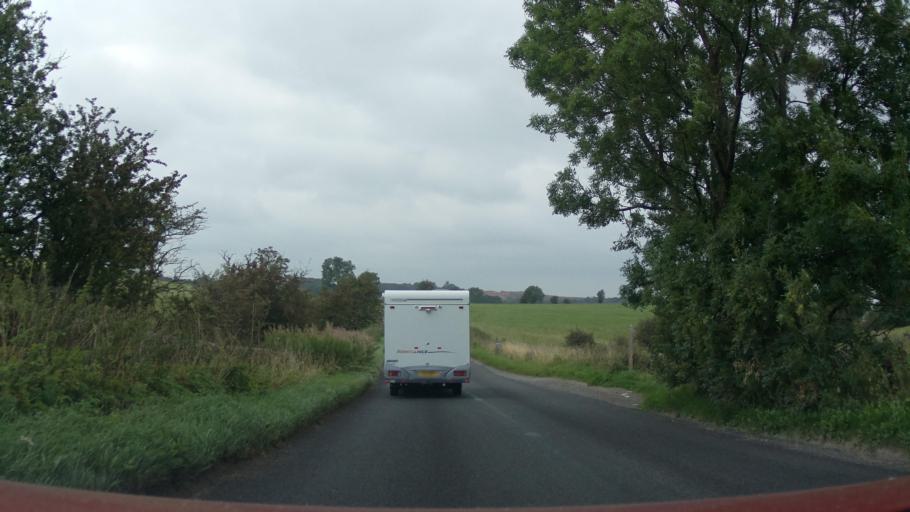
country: GB
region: England
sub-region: Staffordshire
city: Mayfield
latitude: 53.0266
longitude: -1.8536
